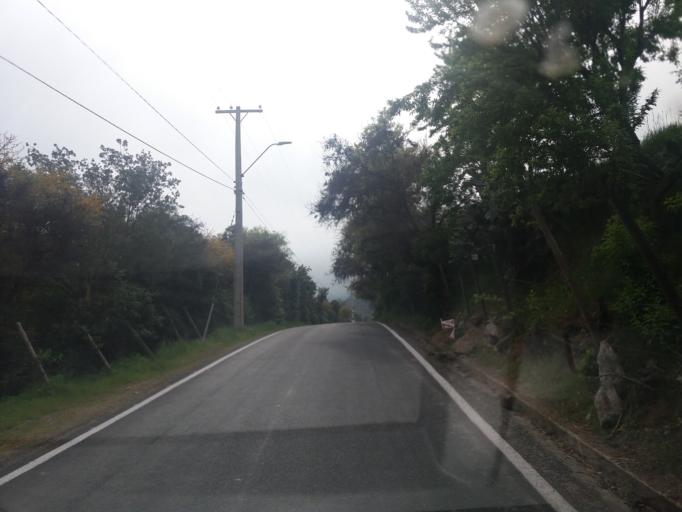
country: CL
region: Valparaiso
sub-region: Provincia de Marga Marga
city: Limache
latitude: -33.0267
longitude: -71.0774
